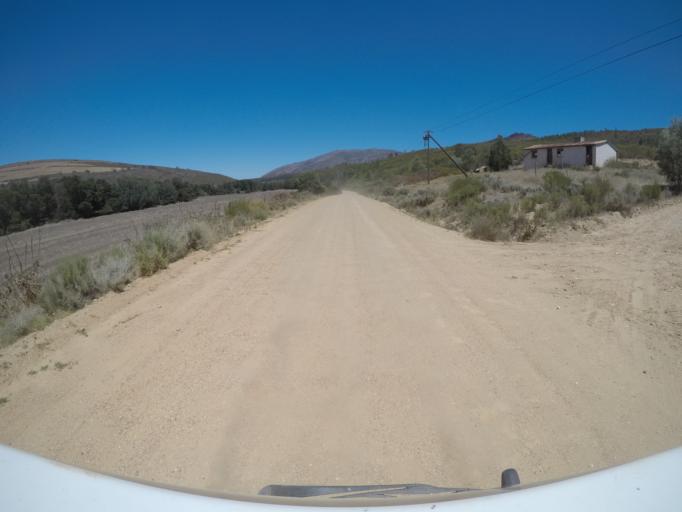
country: ZA
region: Western Cape
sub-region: Overberg District Municipality
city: Caledon
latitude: -34.1513
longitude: 19.2340
